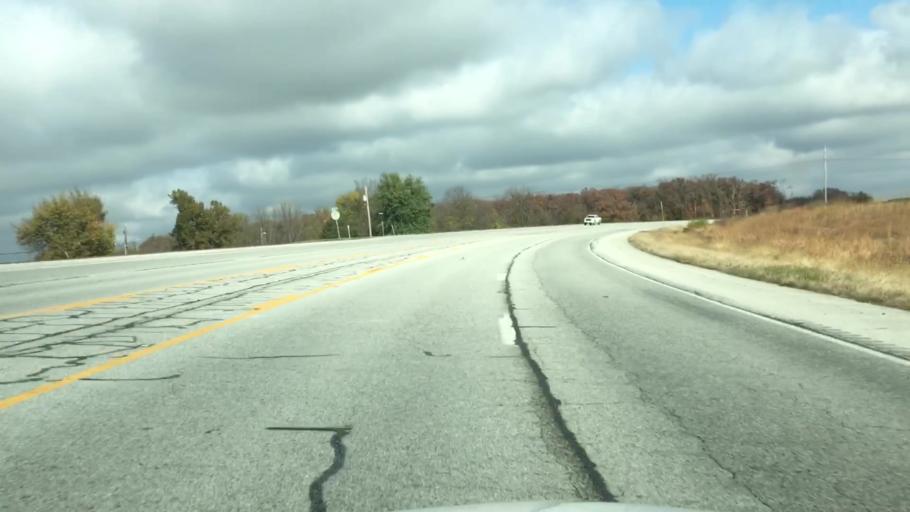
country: US
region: Arkansas
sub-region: Benton County
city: Gentry
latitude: 36.2305
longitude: -94.4948
